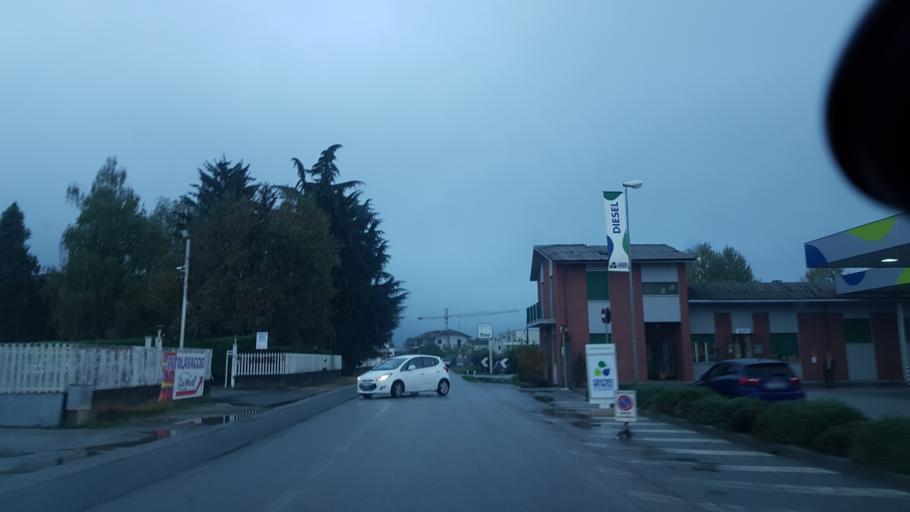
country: IT
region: Piedmont
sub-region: Provincia di Cuneo
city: Fossano
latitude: 44.5545
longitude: 7.7131
